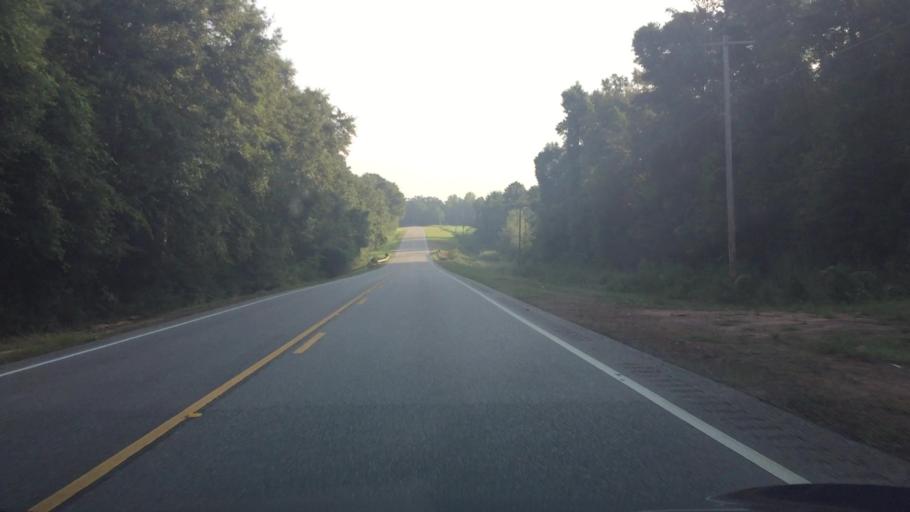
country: US
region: Alabama
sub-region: Covington County
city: Andalusia
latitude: 31.1484
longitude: -86.4592
